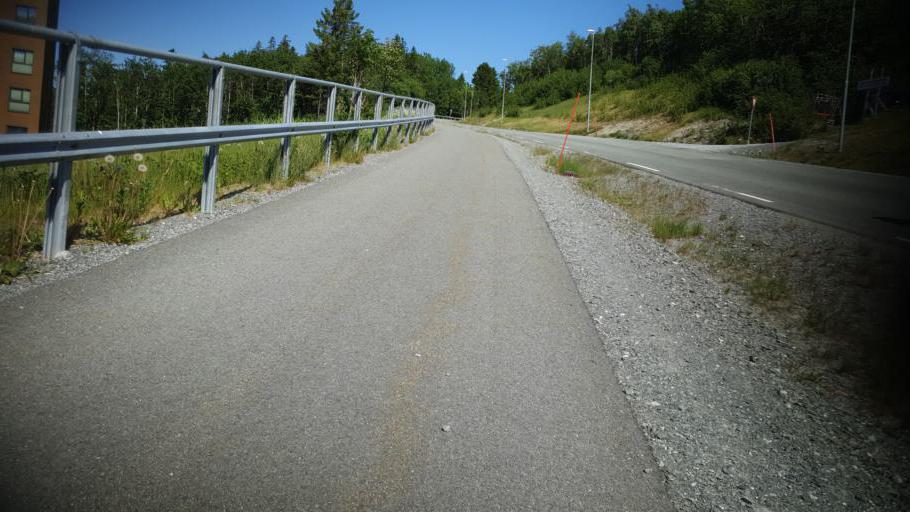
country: NO
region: Sor-Trondelag
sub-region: Malvik
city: Malvik
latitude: 63.4312
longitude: 10.5878
